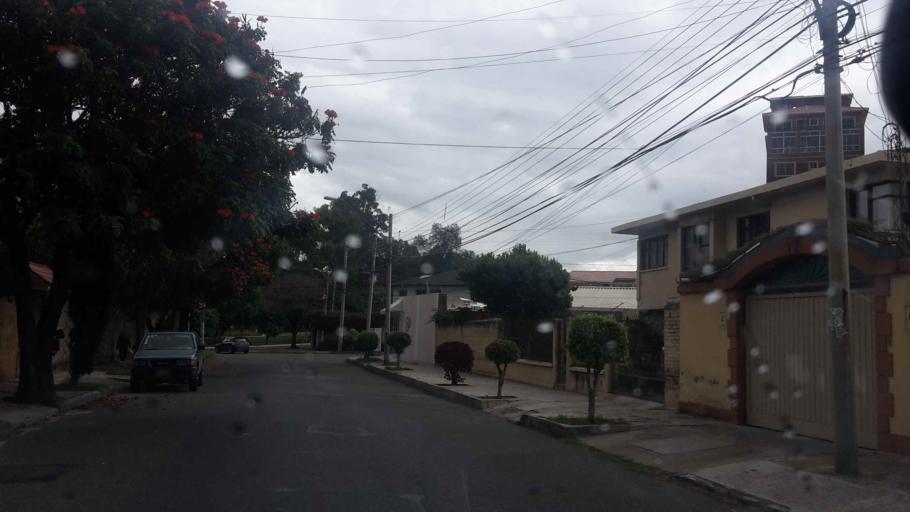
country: BO
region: Cochabamba
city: Cochabamba
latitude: -17.3690
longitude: -66.1697
